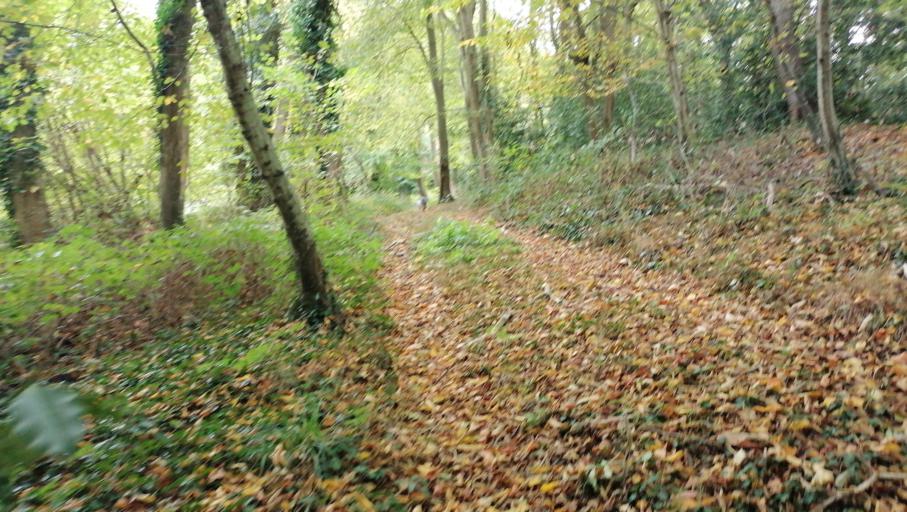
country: FR
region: Picardie
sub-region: Departement de la Somme
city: Bouttencourt
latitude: 49.8924
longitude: 1.6779
